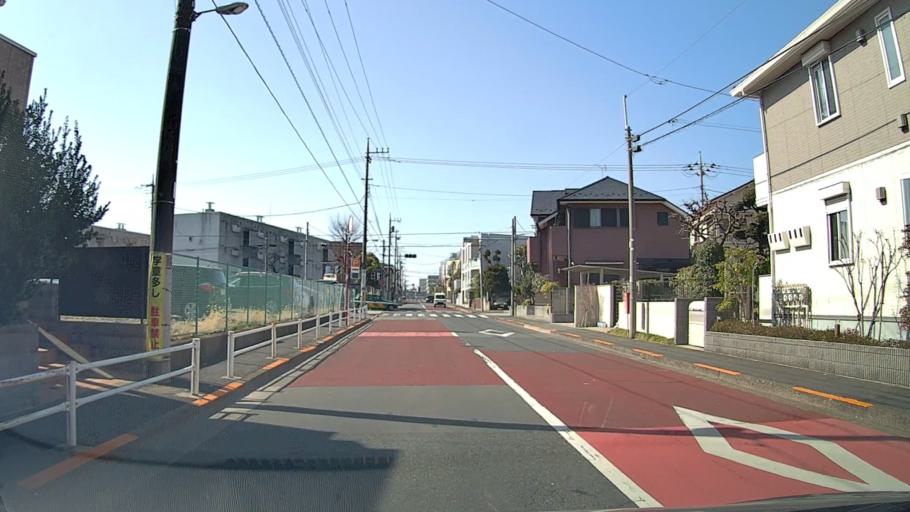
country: JP
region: Tokyo
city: Tokyo
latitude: 35.7308
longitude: 139.6726
